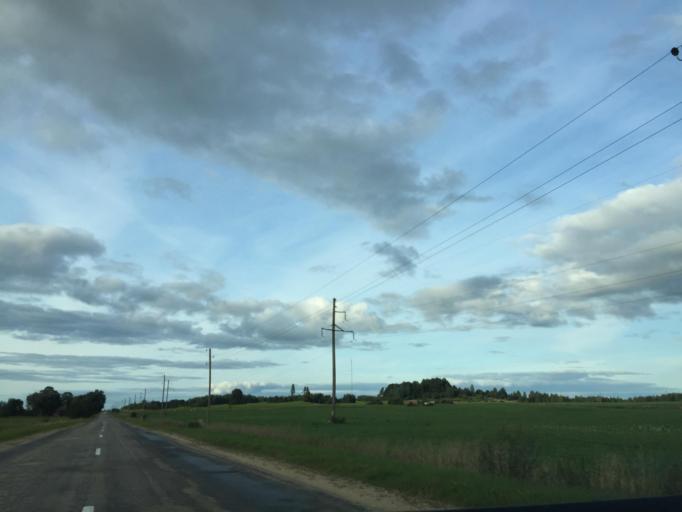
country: LV
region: Nereta
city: Nereta
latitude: 56.2214
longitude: 25.3184
